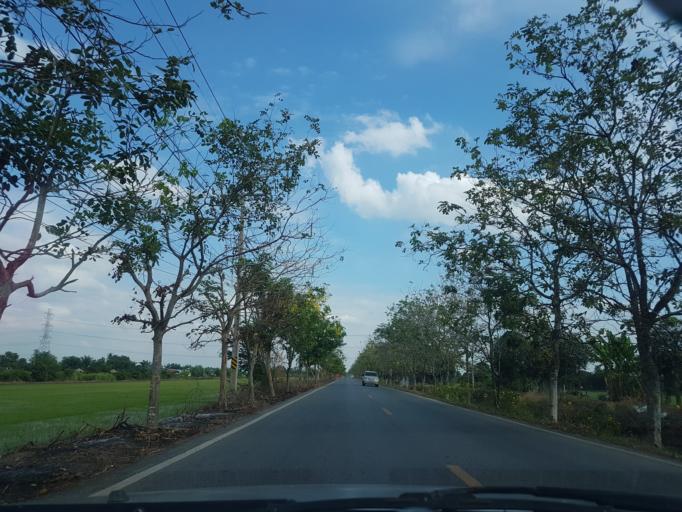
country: TH
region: Pathum Thani
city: Nong Suea
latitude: 14.1358
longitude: 100.8756
